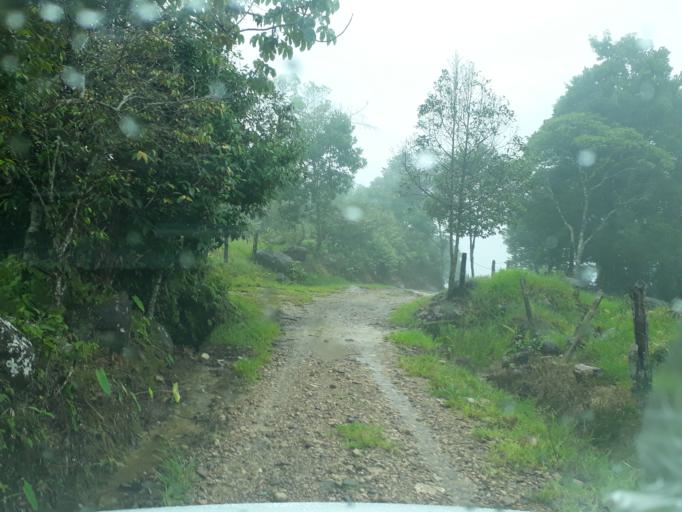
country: CO
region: Cundinamarca
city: Medina
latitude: 4.5312
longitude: -73.3766
